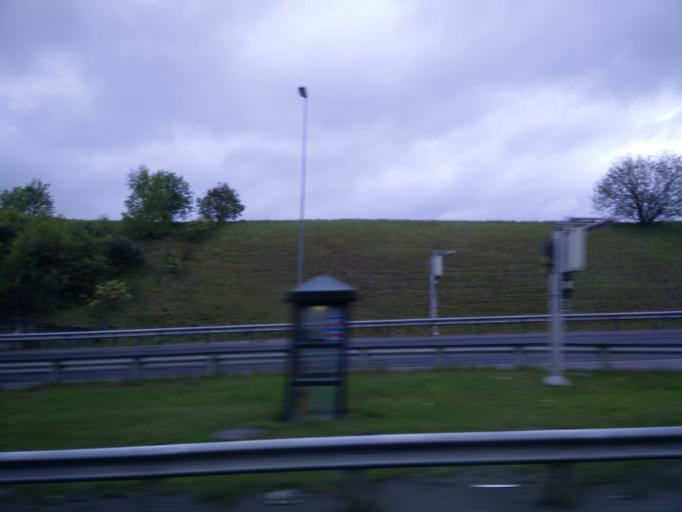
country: NO
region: Sor-Trondelag
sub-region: Trondheim
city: Trondheim
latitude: 63.4300
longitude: 10.4979
